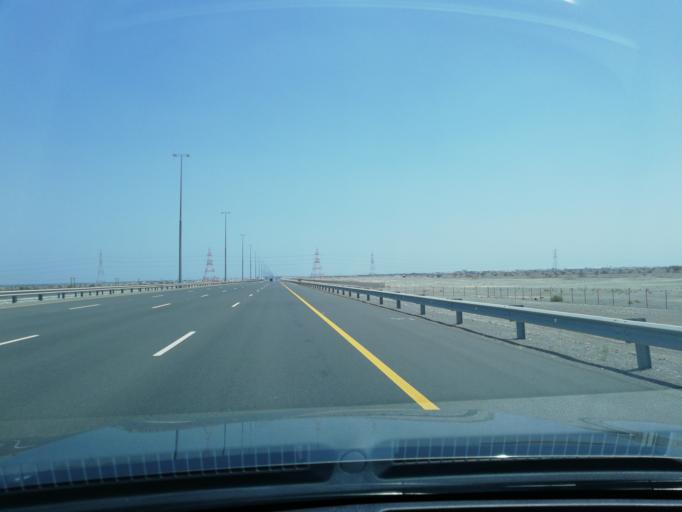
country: OM
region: Al Batinah
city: Barka'
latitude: 23.6066
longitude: 57.8246
